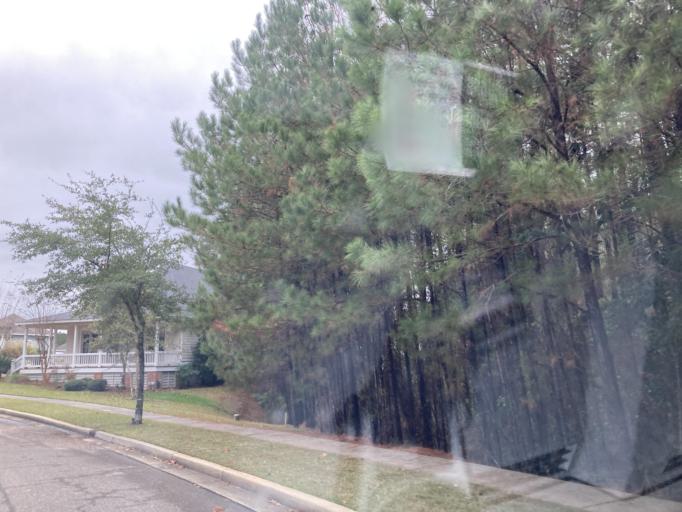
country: US
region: Mississippi
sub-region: Lamar County
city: West Hattiesburg
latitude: 31.2849
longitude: -89.4726
